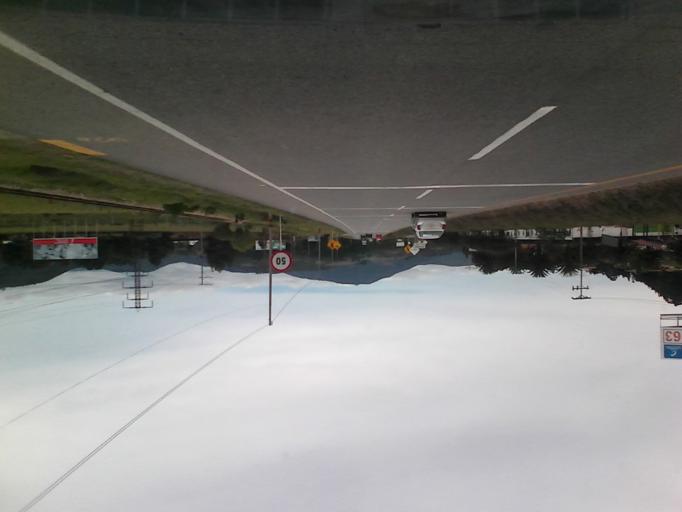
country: CO
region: Boyaca
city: Duitama
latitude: 5.7898
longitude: -73.0556
